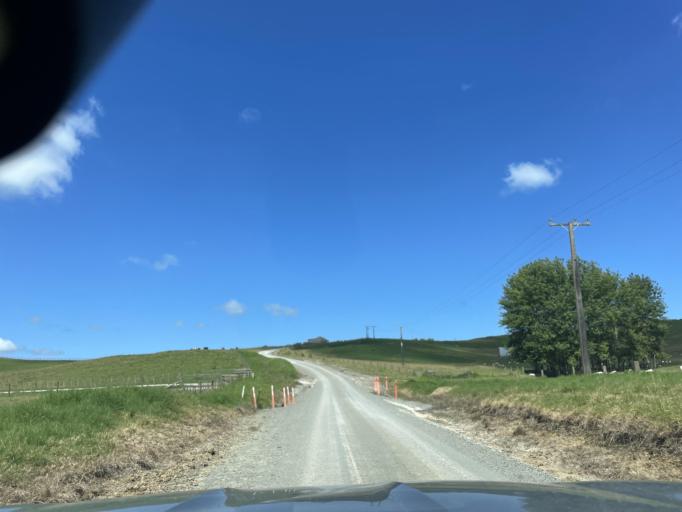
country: NZ
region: Auckland
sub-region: Auckland
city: Wellsford
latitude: -36.2855
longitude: 174.3544
